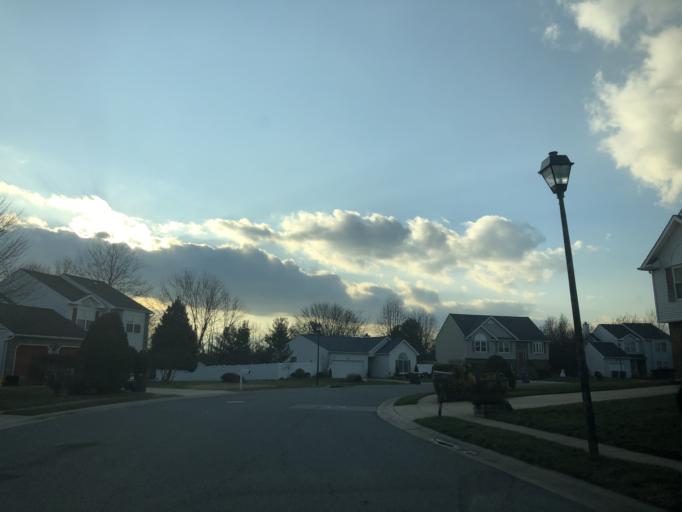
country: US
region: Delaware
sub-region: New Castle County
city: Bear
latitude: 39.6281
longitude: -75.6490
